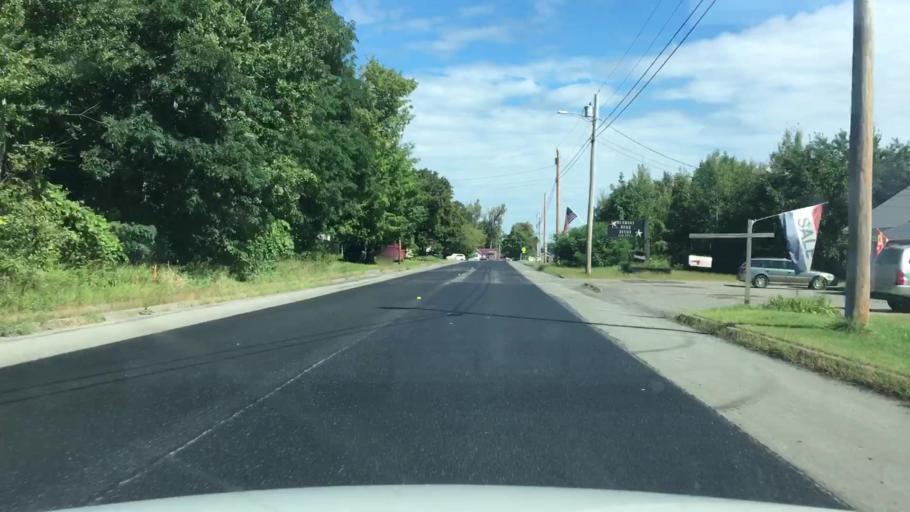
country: US
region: Maine
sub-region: Penobscot County
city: Corinna
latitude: 44.9147
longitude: -69.2635
